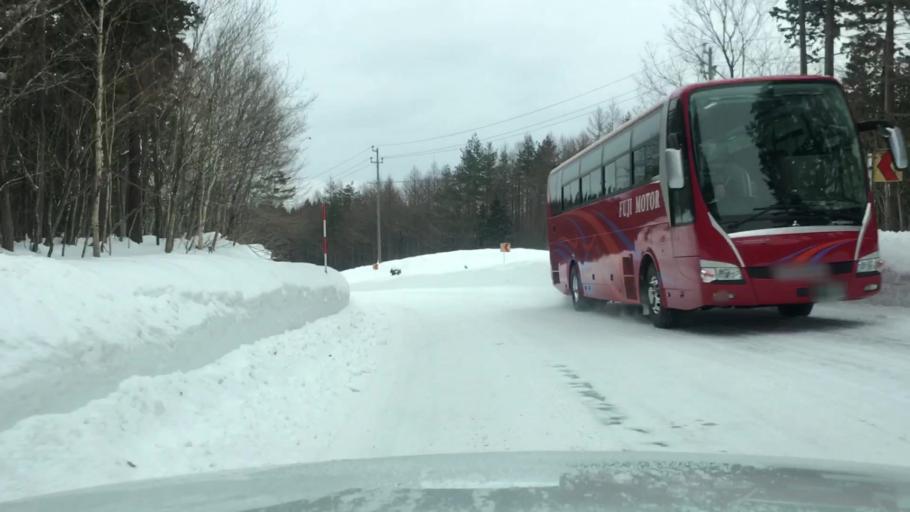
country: JP
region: Iwate
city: Shizukuishi
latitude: 39.9833
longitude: 141.0037
